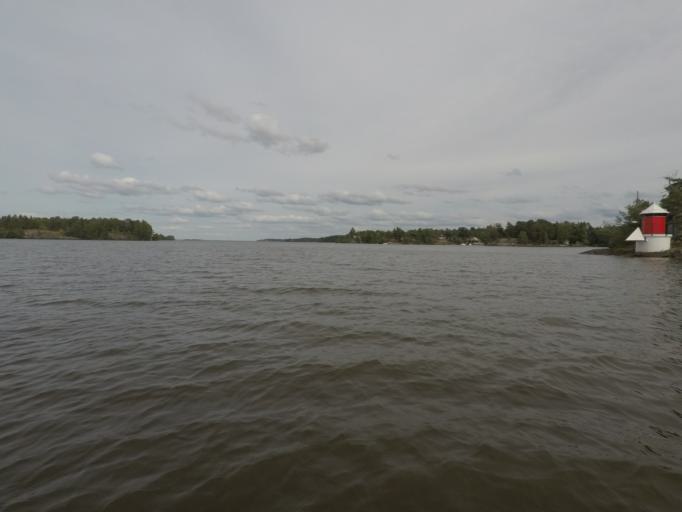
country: SE
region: Soedermanland
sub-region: Eskilstuna Kommun
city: Kvicksund
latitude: 59.4546
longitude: 16.3580
